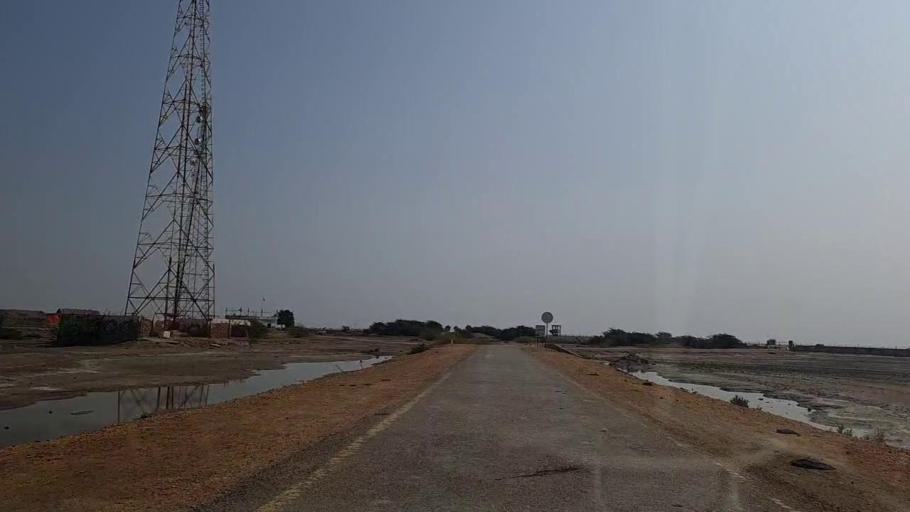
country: PK
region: Sindh
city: Chuhar Jamali
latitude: 24.1652
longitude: 67.8998
